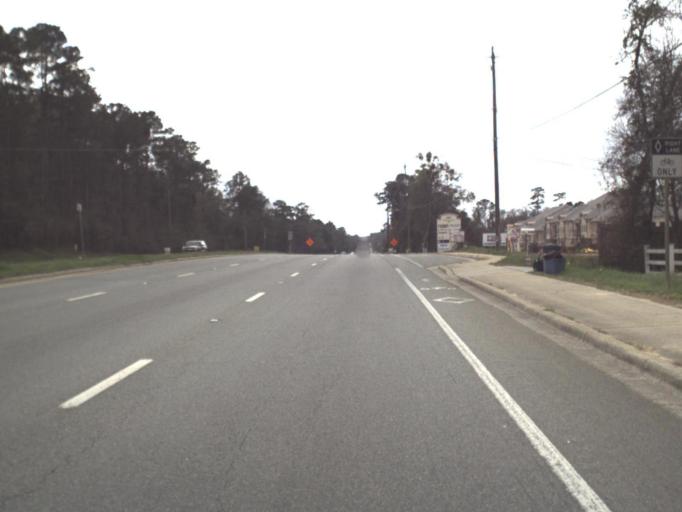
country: US
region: Florida
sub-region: Leon County
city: Tallahassee
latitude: 30.5540
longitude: -84.2223
